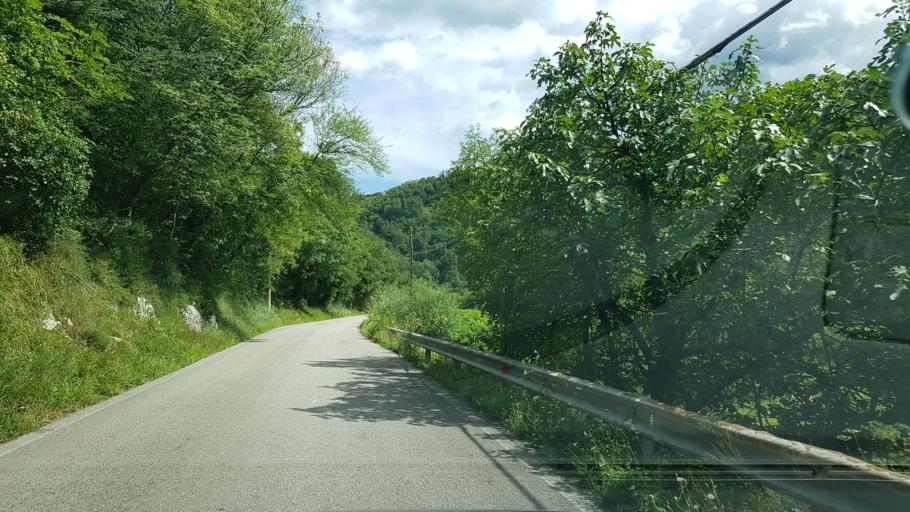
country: IT
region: Friuli Venezia Giulia
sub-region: Provincia di Udine
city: Prepotto
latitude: 46.0628
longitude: 13.5050
